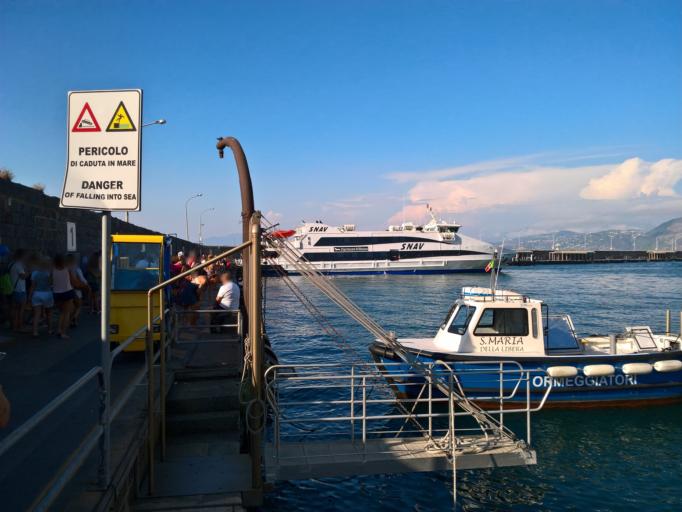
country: IT
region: Campania
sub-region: Provincia di Napoli
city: Capri
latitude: 40.5568
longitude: 14.2391
